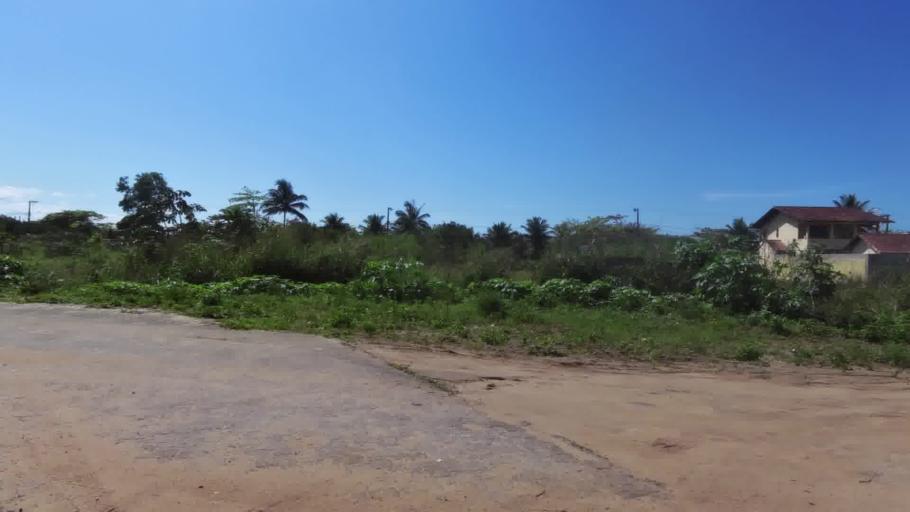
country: BR
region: Espirito Santo
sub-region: Piuma
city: Piuma
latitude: -20.8296
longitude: -40.6209
